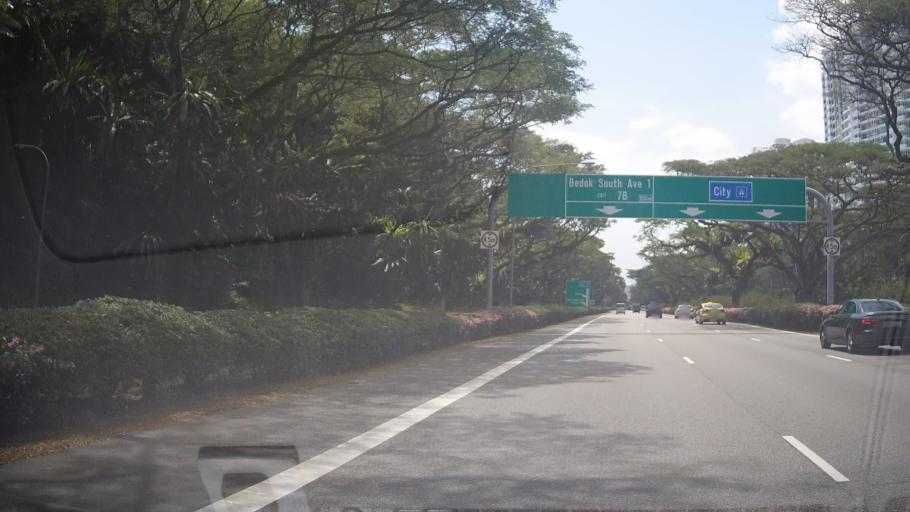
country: SG
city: Singapore
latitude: 1.3112
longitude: 103.9427
